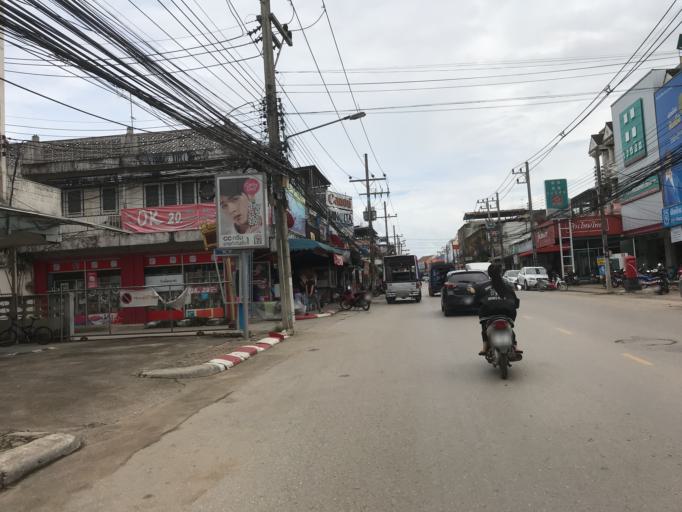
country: TH
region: Chiang Rai
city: Chiang Rai
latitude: 19.8920
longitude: 99.8308
